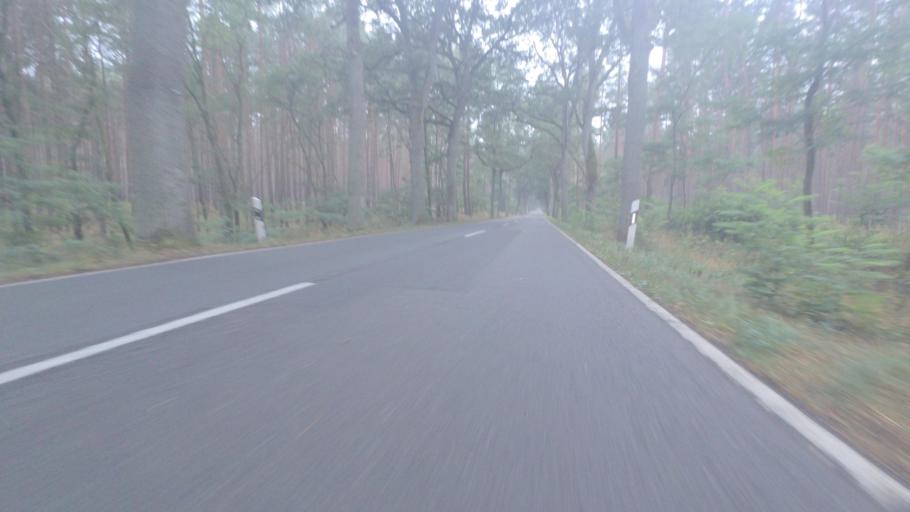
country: DE
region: Brandenburg
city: Heiligengrabe
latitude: 53.1030
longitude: 12.3669
